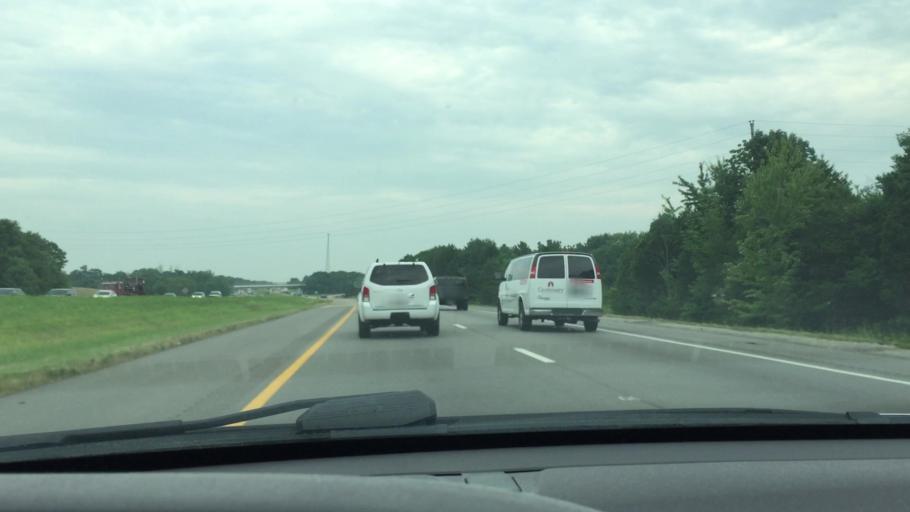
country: US
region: Ohio
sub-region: Warren County
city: Morrow
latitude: 39.4257
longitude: -84.0855
